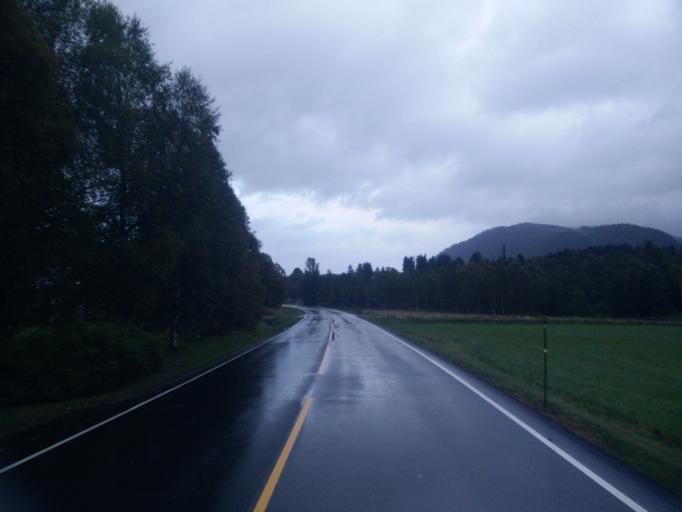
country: NO
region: More og Romsdal
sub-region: Rindal
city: Rindal
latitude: 63.0157
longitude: 9.0718
